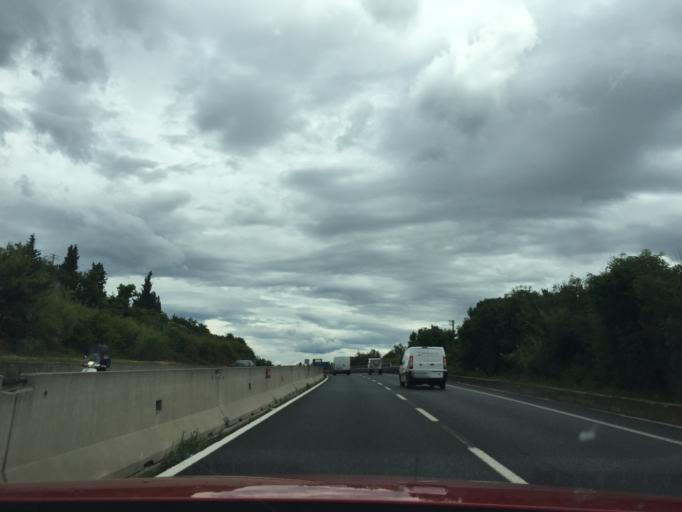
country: IT
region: Tuscany
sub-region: Province of Florence
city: Quattro Strade
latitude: 43.7327
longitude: 11.1034
